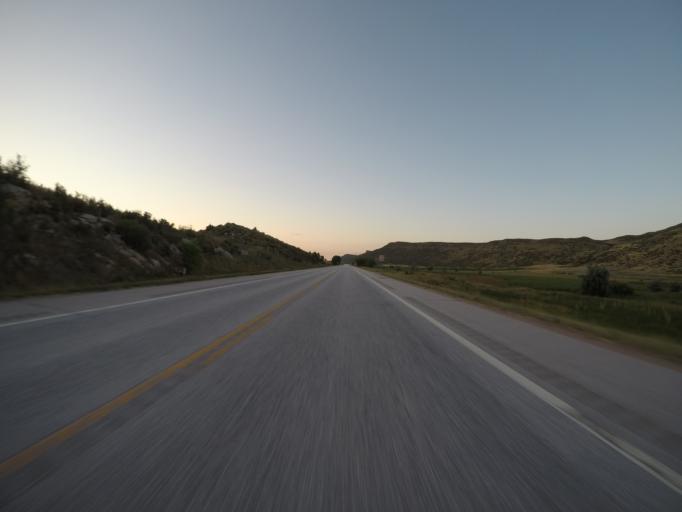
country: US
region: Colorado
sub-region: Larimer County
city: Laporte
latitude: 40.6799
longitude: -105.1783
